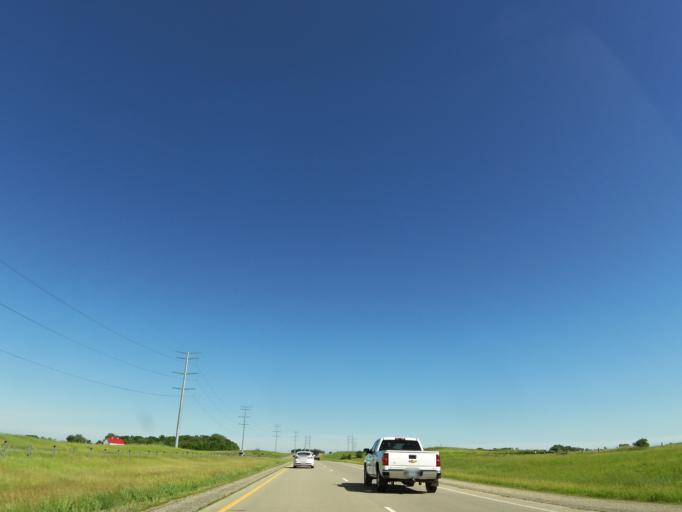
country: US
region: Minnesota
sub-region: Otter Tail County
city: Pelican Rapids
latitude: 46.4557
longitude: -96.2503
